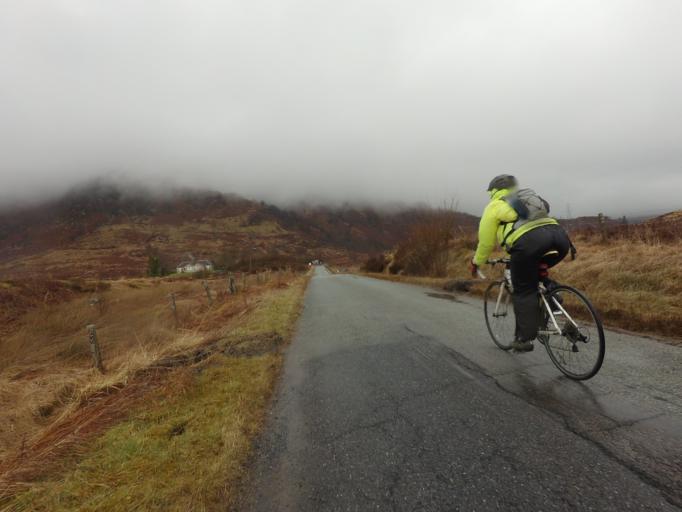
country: GB
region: Scotland
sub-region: West Dunbartonshire
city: Balloch
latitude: 56.2520
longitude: -4.5887
